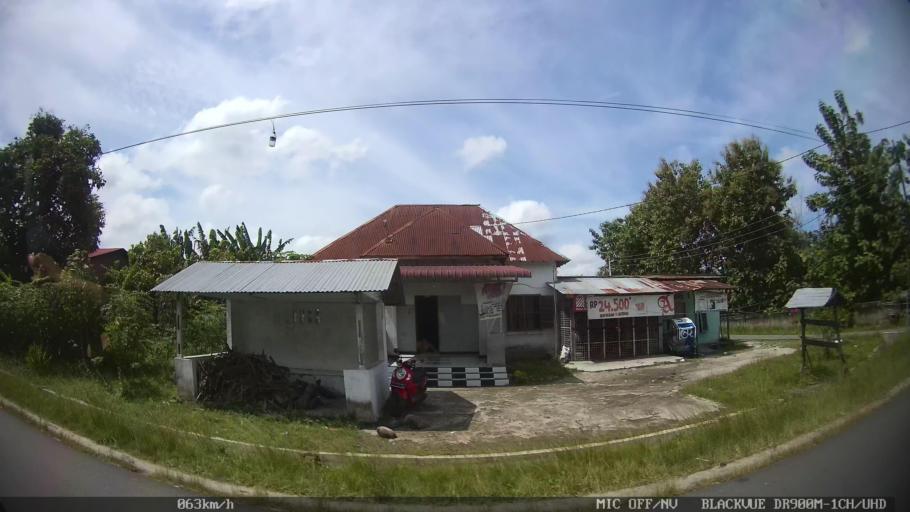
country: ID
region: North Sumatra
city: Percut
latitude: 3.5891
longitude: 98.8800
